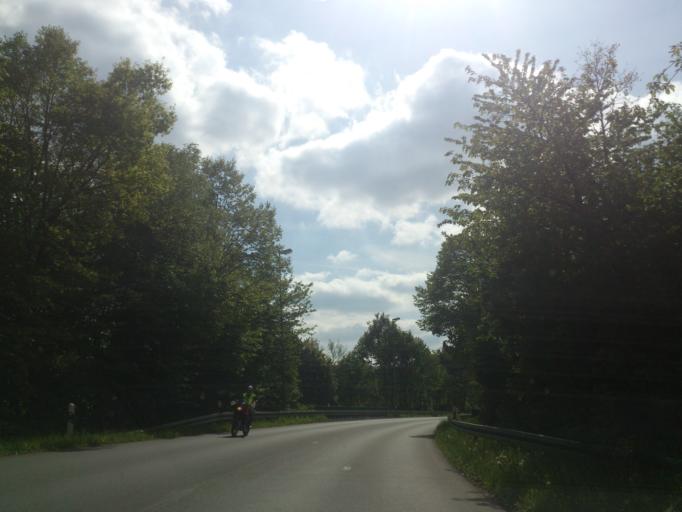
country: DE
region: North Rhine-Westphalia
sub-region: Regierungsbezirk Detmold
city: Bad Driburg
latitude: 51.7311
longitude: 9.0212
